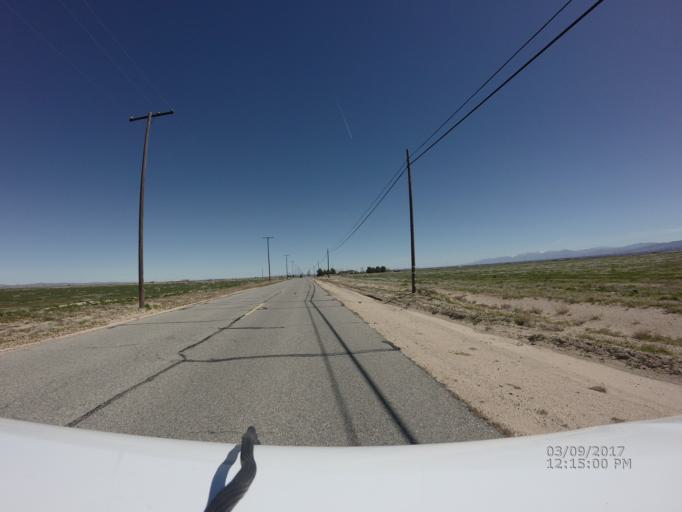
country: US
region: California
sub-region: Los Angeles County
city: Quartz Hill
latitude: 34.7330
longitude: -118.2744
